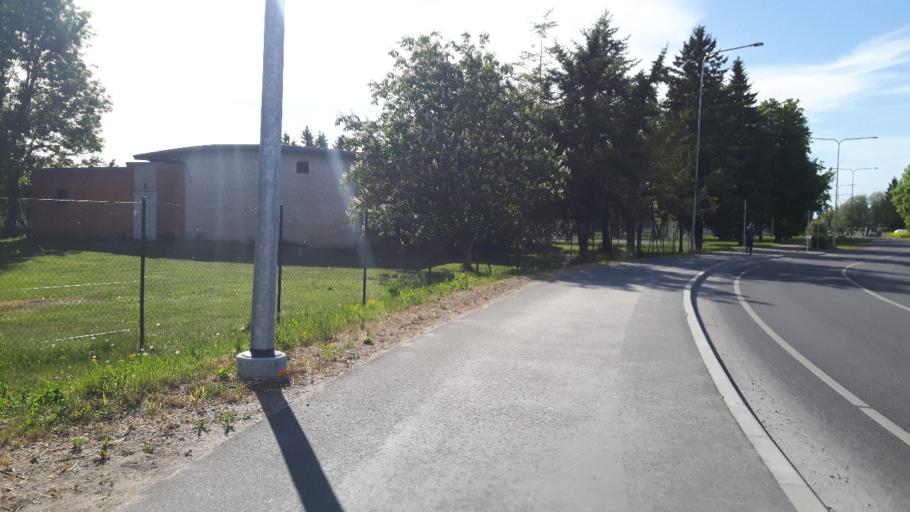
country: EE
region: Harju
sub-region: Joelaehtme vald
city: Loo
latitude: 59.4315
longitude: 24.9536
